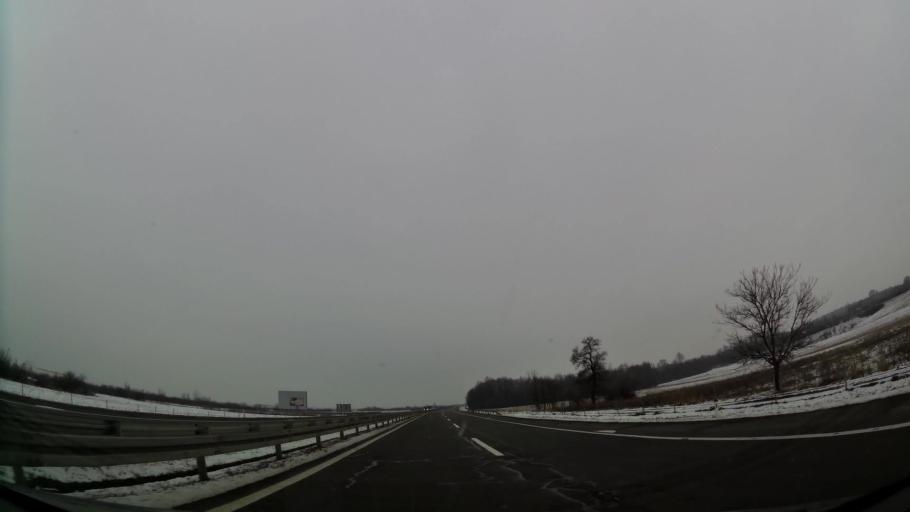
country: RS
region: Central Serbia
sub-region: Pomoravski Okrug
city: Paracin
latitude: 43.8876
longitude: 21.3989
